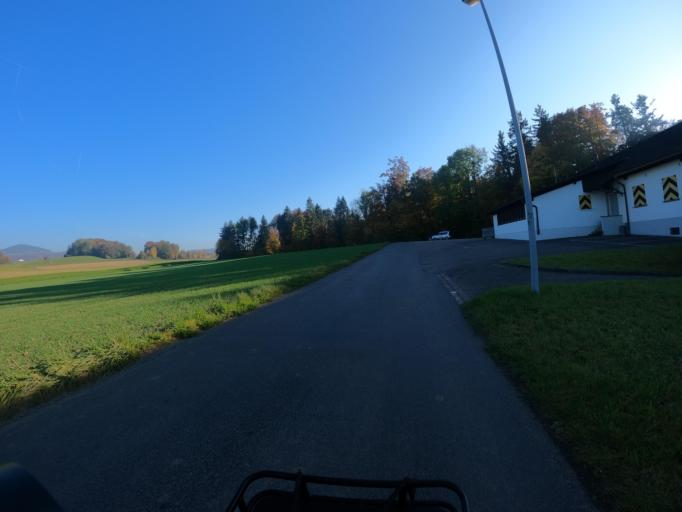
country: CH
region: Zurich
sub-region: Bezirk Affoltern
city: Obfelden / Toussen
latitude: 47.2815
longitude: 8.4319
